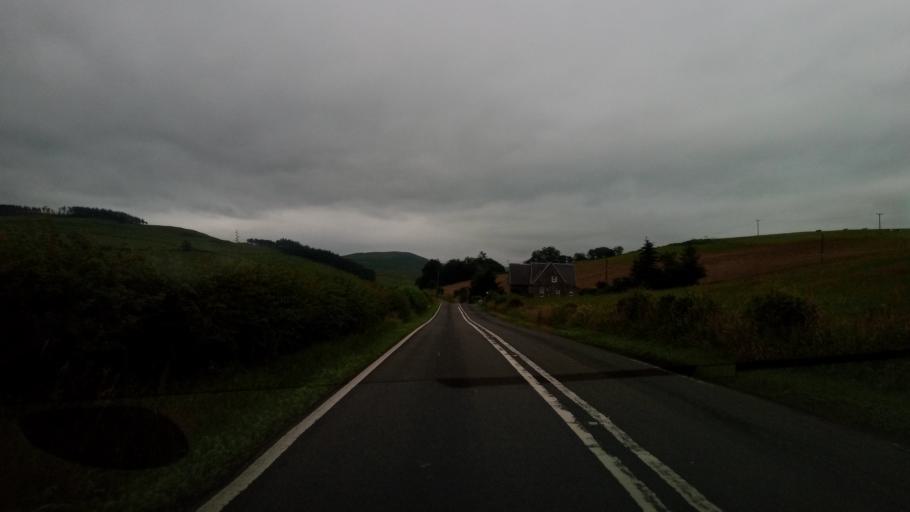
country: GB
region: Scotland
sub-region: The Scottish Borders
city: Hawick
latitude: 55.3721
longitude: -2.8779
